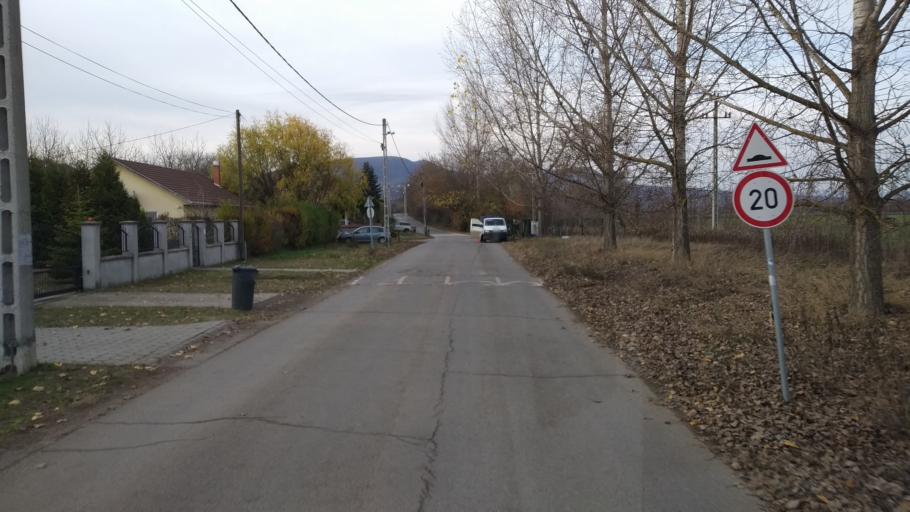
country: HU
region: Pest
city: God
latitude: 47.6868
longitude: 19.1123
